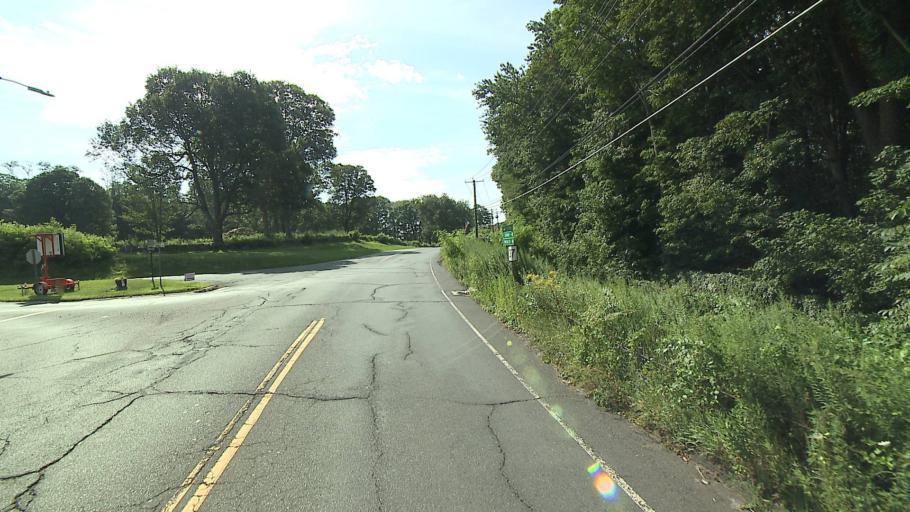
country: US
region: New York
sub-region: Putnam County
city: Putnam Lake
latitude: 41.4647
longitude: -73.4822
